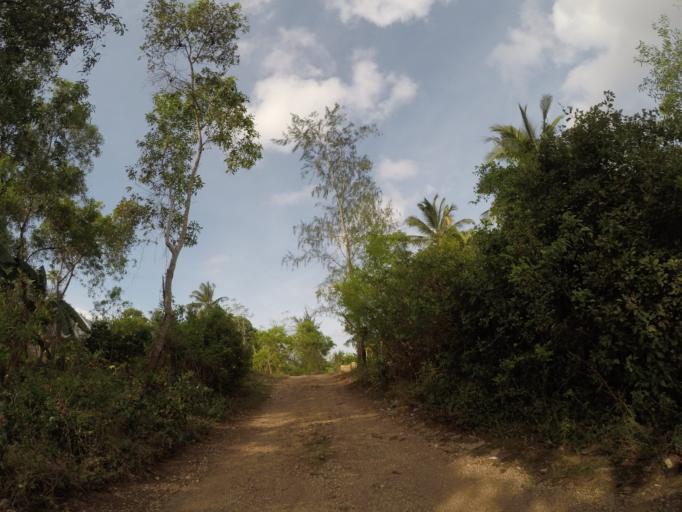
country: TZ
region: Zanzibar Central/South
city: Koani
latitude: -6.2203
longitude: 39.3201
